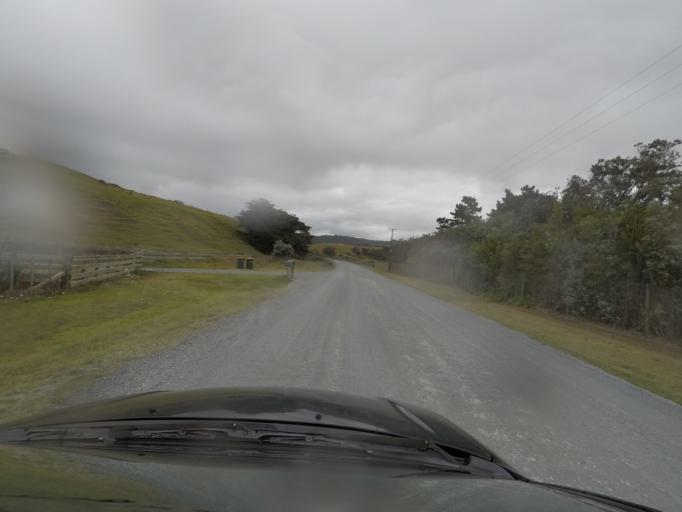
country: NZ
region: Auckland
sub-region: Auckland
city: Warkworth
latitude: -36.2461
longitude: 174.7218
